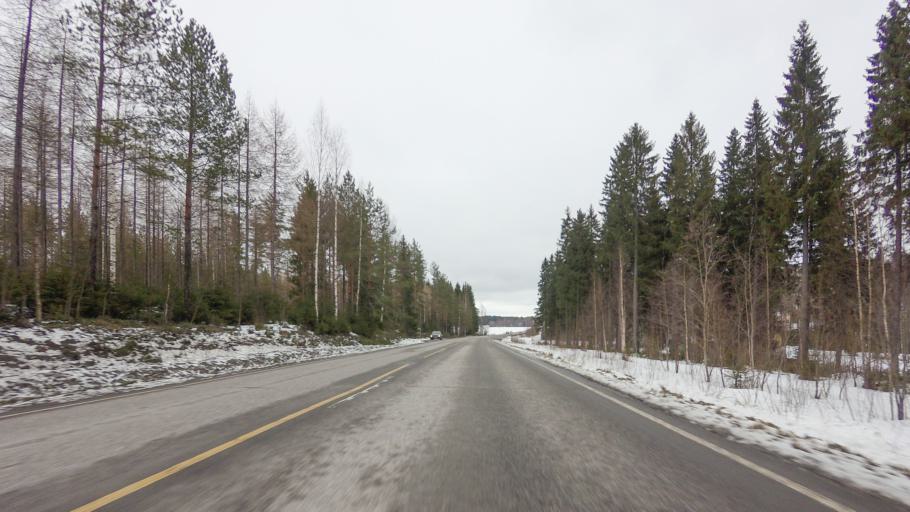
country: FI
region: Southern Savonia
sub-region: Savonlinna
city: Savonlinna
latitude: 61.8886
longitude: 28.9322
